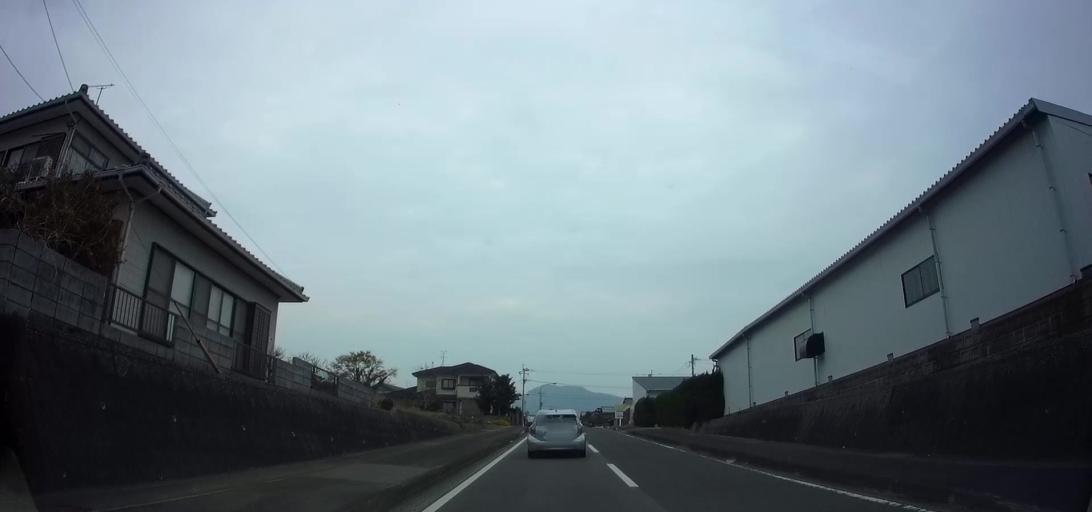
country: JP
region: Nagasaki
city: Shimabara
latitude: 32.6612
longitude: 130.2879
